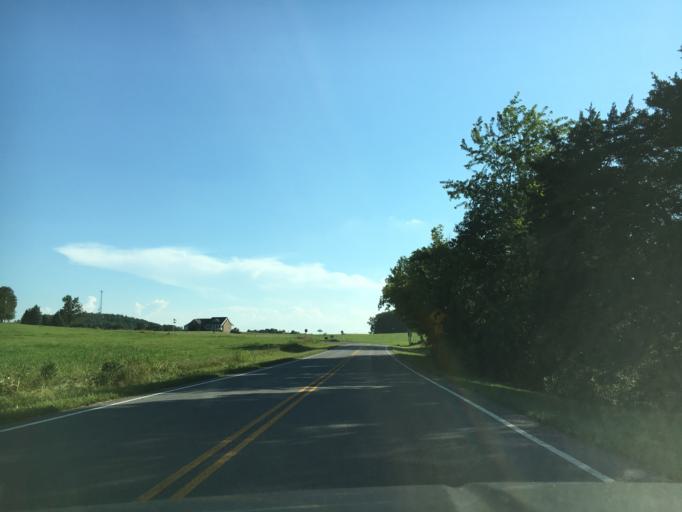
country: US
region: Virginia
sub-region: City of Bedford
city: Bedford
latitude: 37.2198
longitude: -79.4773
